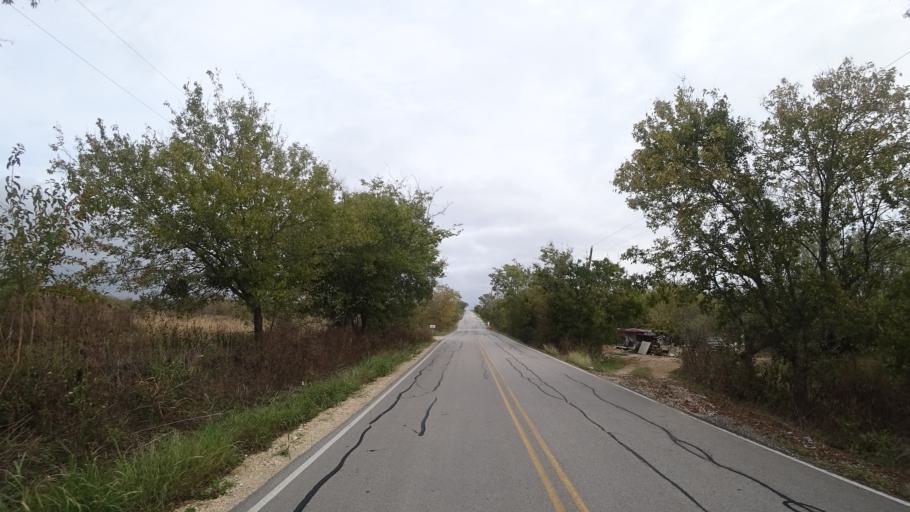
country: US
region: Texas
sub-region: Travis County
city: Manor
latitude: 30.3780
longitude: -97.5596
